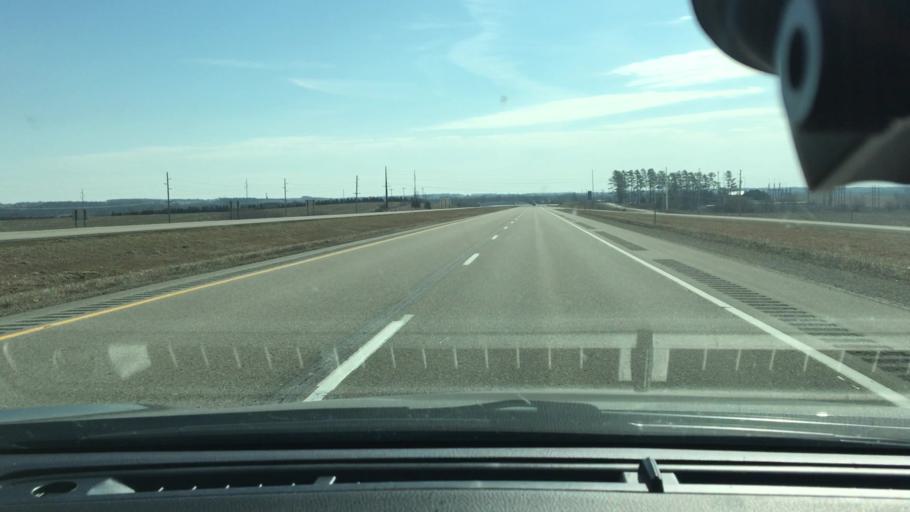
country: US
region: Iowa
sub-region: Floyd County
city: Charles City
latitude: 43.0387
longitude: -92.6705
